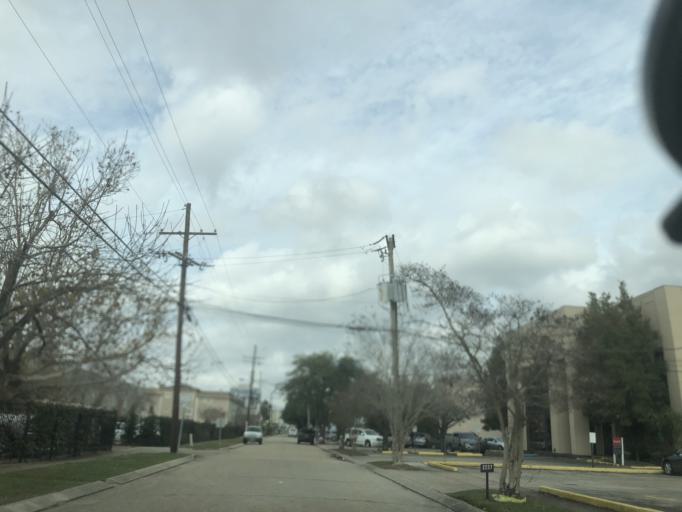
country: US
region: Louisiana
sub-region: Jefferson Parish
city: Metairie
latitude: 29.9939
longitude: -90.1586
